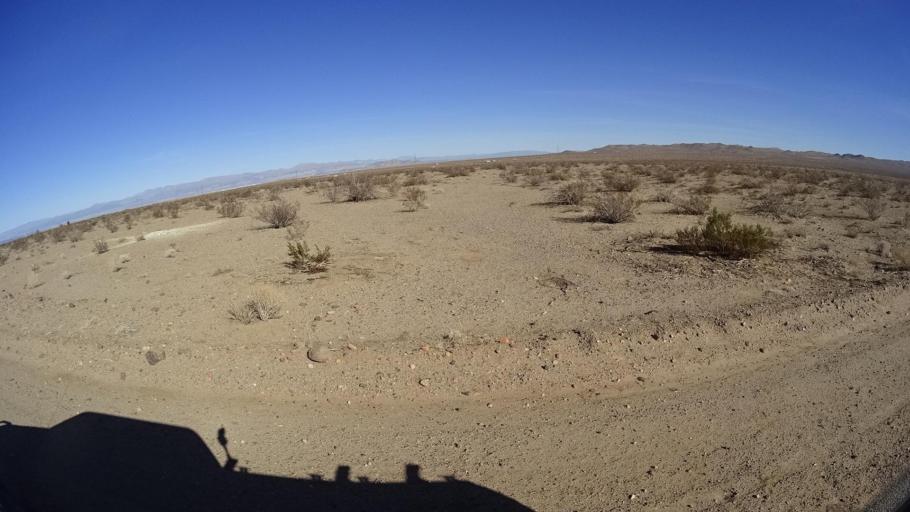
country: US
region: California
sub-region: Kern County
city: China Lake Acres
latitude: 35.5643
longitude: -117.7772
